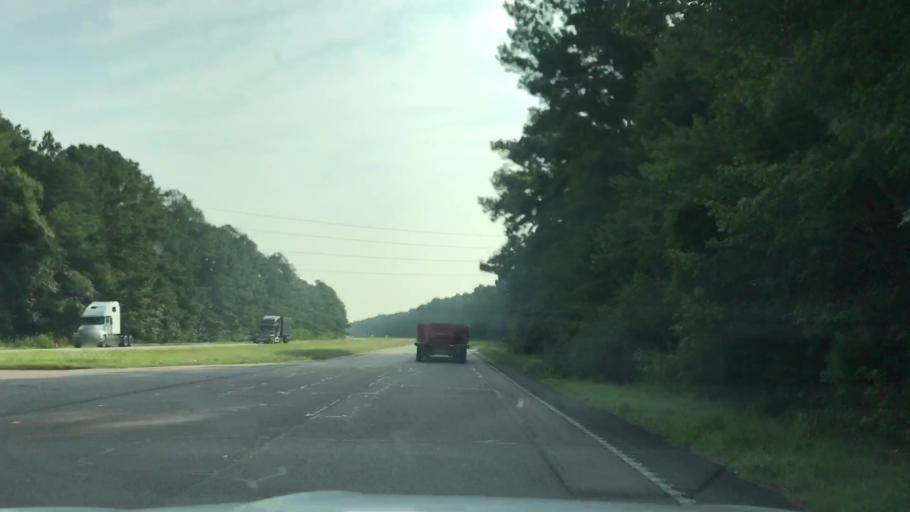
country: US
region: South Carolina
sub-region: Charleston County
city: Awendaw
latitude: 33.0784
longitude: -79.5065
